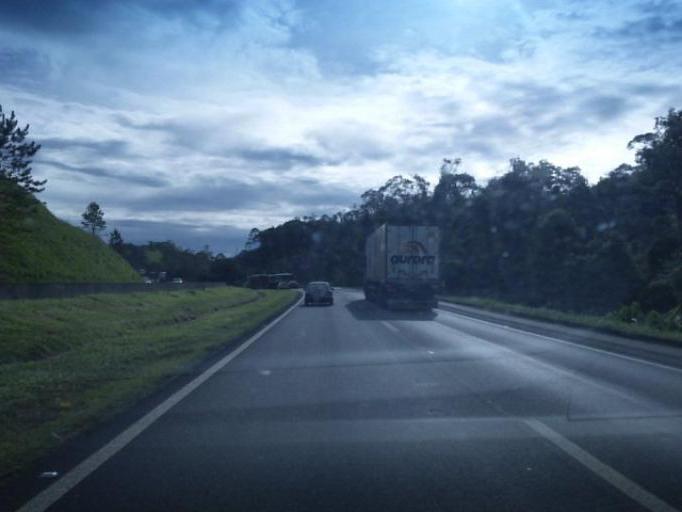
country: BR
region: Parana
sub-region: Antonina
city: Antonina
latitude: -25.1031
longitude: -48.7369
